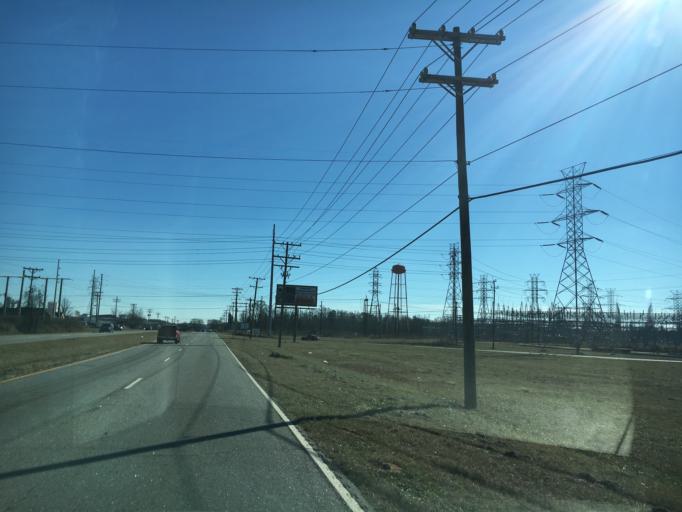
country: US
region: South Carolina
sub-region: Anderson County
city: Homeland Park
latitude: 34.4416
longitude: -82.6660
